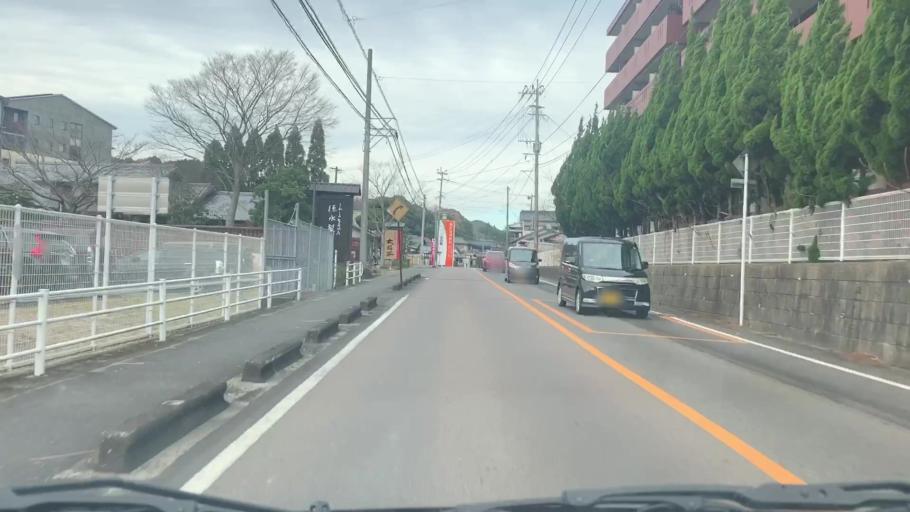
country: JP
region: Saga Prefecture
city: Ureshinomachi-shimojuku
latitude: 33.1010
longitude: 129.9789
